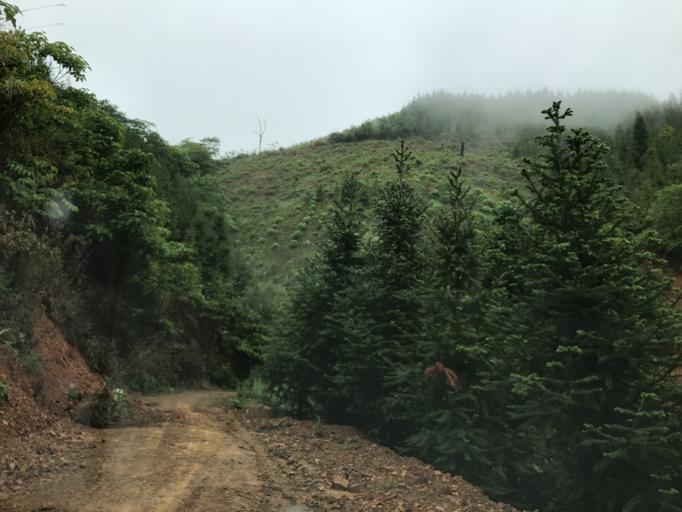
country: CN
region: Guangxi Zhuangzu Zizhiqu
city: Leli
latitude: 24.8049
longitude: 106.0789
